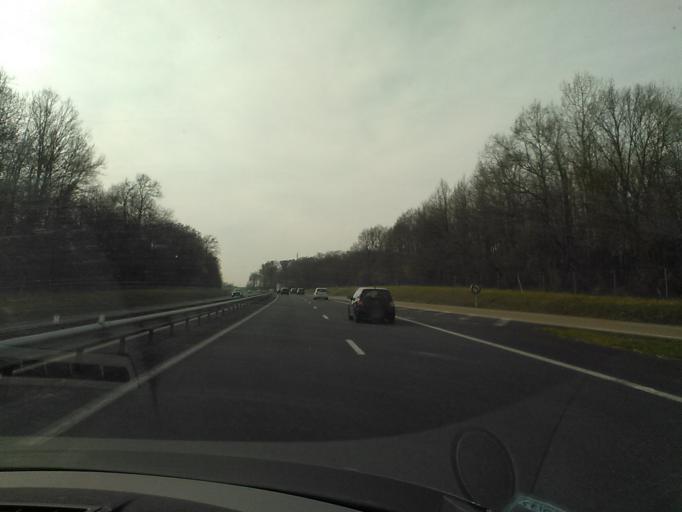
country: FR
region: Champagne-Ardenne
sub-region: Departement de l'Aube
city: Verrieres
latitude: 48.2292
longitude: 4.1765
